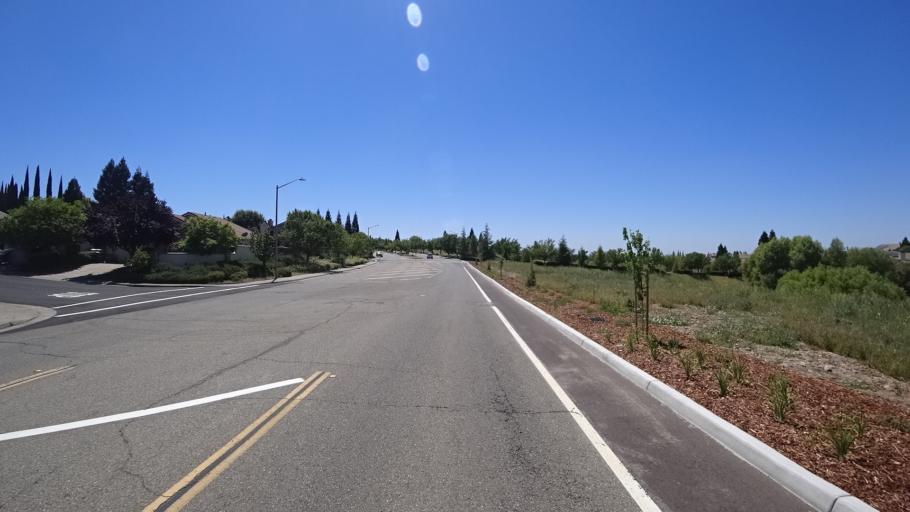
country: US
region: California
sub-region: Placer County
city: Rocklin
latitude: 38.8233
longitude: -121.2706
